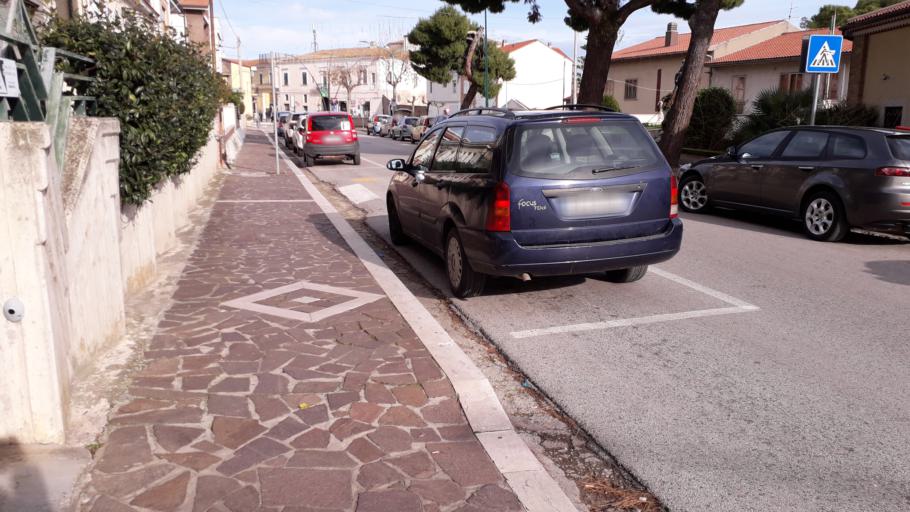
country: IT
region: Molise
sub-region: Provincia di Campobasso
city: Campomarino
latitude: 41.9560
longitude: 15.0356
